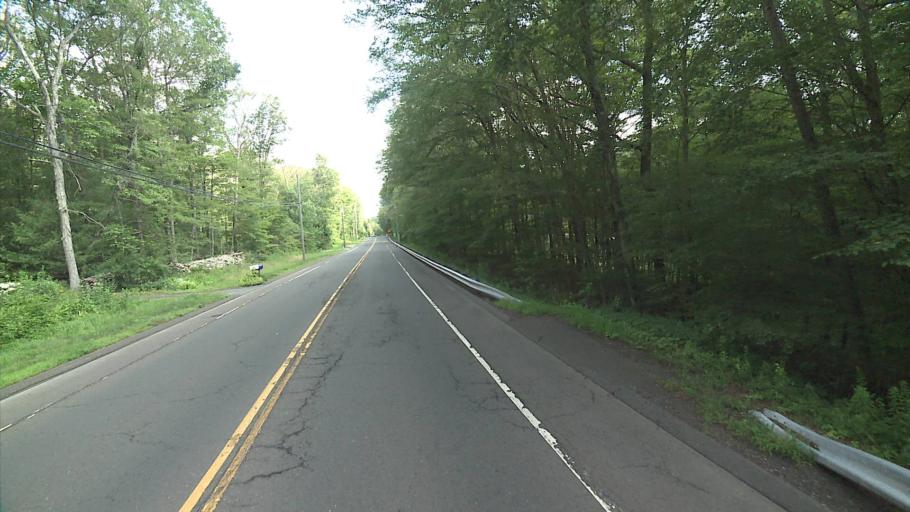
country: US
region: Connecticut
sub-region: Middlesex County
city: Chester Center
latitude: 41.3555
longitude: -72.4986
